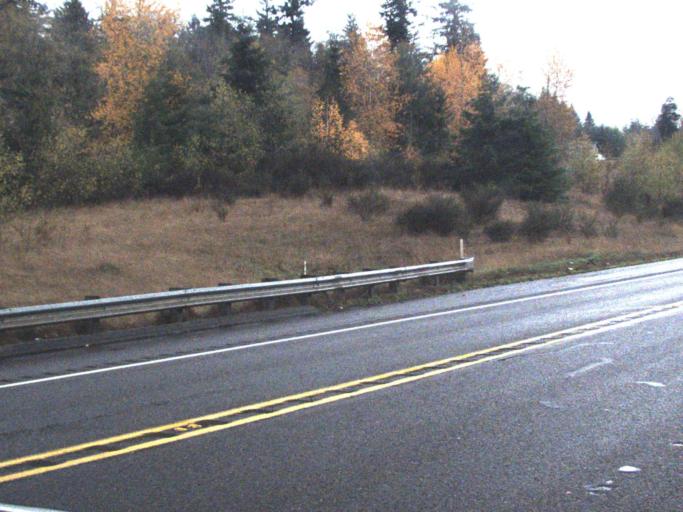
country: US
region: Washington
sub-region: Snohomish County
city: Fobes Hill
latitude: 47.9537
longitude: -122.1122
